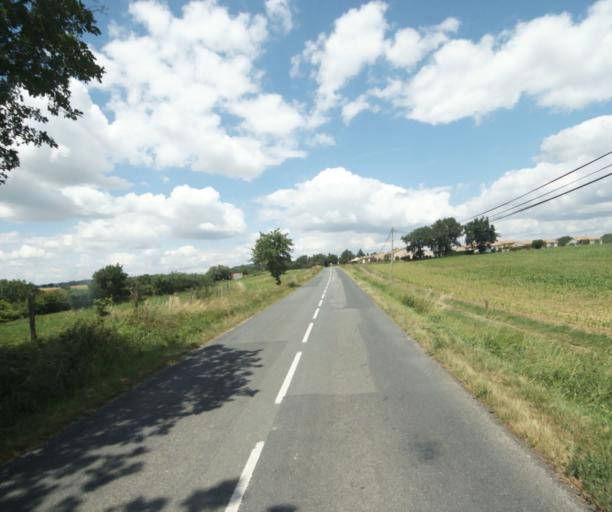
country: FR
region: Midi-Pyrenees
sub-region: Departement du Tarn
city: Soual
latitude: 43.5320
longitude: 2.0618
